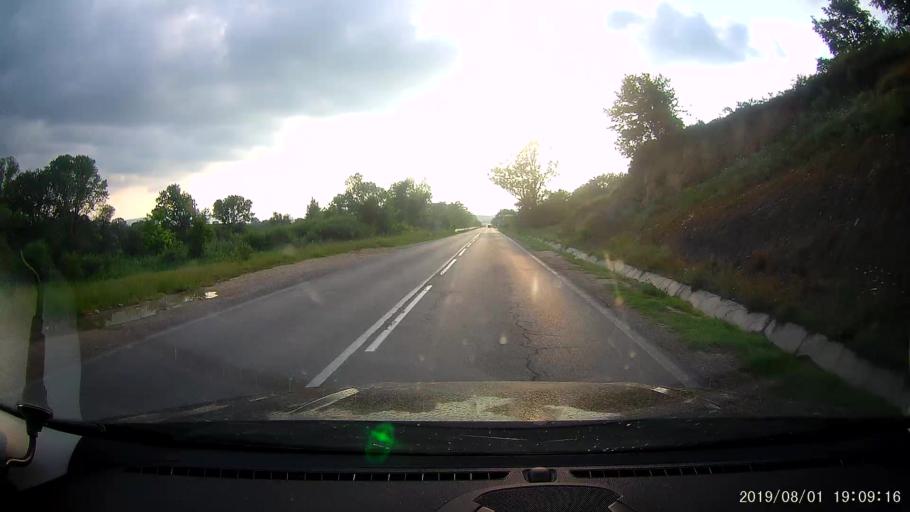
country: BG
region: Shumen
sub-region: Obshtina Smyadovo
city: Smyadovo
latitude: 42.9837
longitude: 27.0079
